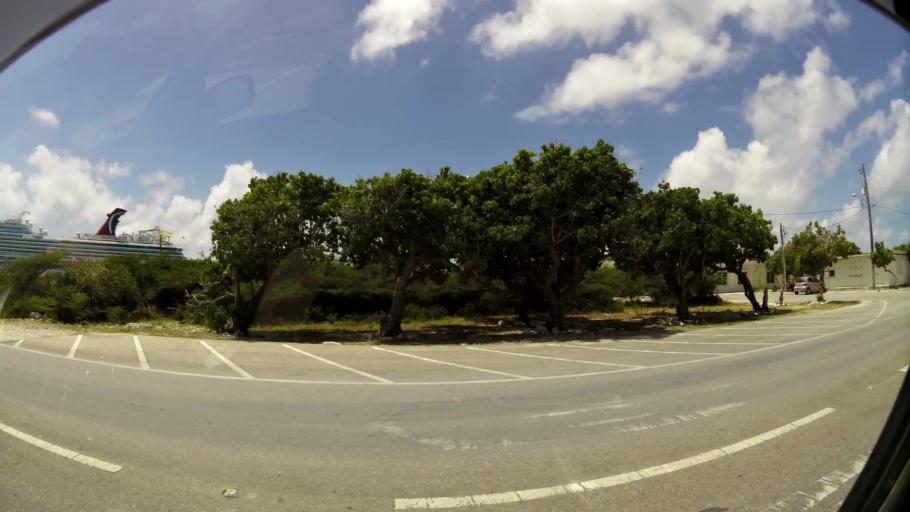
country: TC
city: Cockburn Town
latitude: 21.4314
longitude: -71.1454
